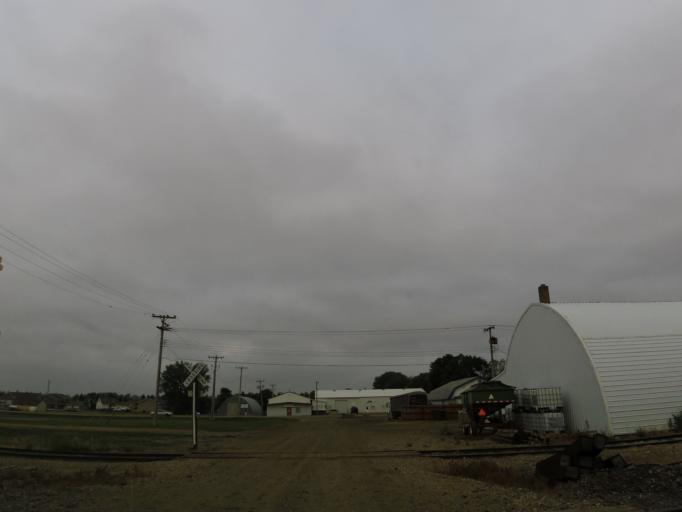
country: US
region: North Dakota
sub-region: Walsh County
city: Grafton
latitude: 48.5681
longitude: -97.1793
